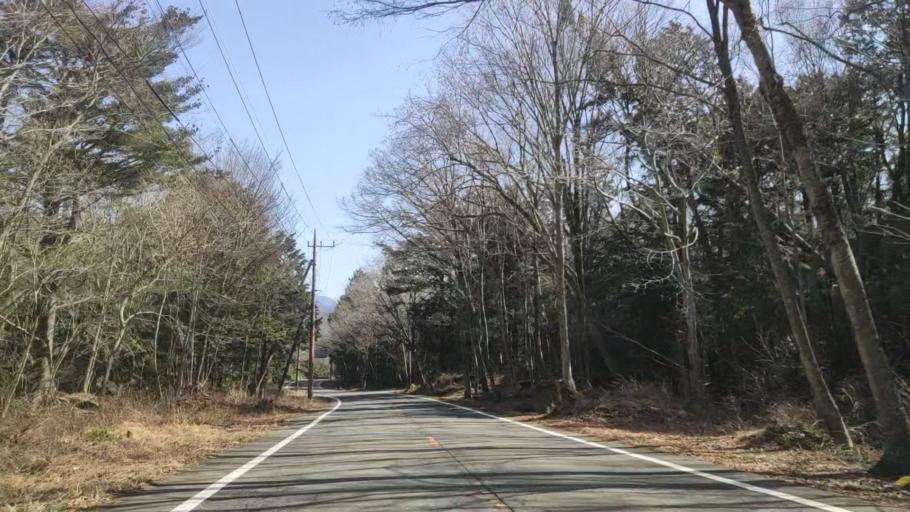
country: JP
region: Yamanashi
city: Fujikawaguchiko
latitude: 35.4799
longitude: 138.6597
